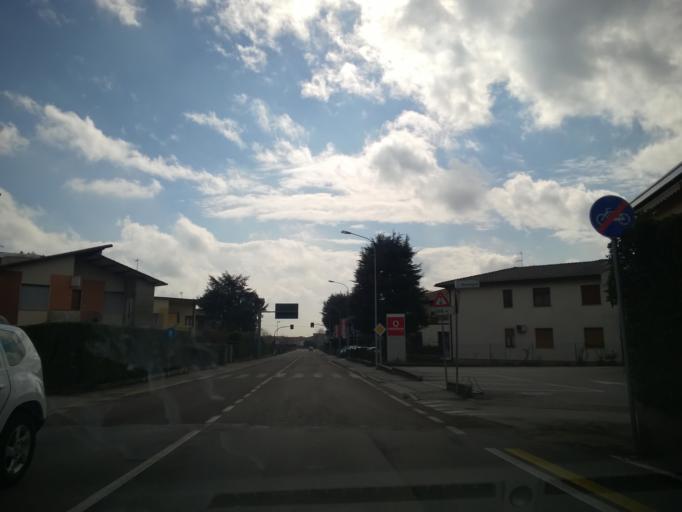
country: IT
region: Veneto
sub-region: Provincia di Vicenza
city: Thiene
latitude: 45.7108
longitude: 11.4672
